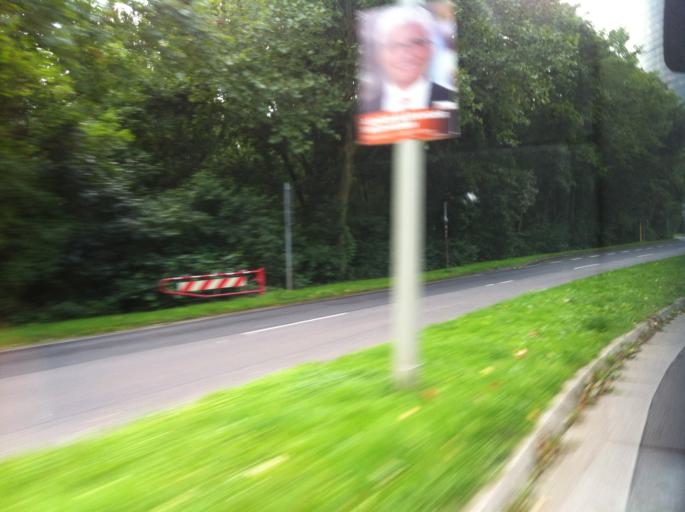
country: DE
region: North Rhine-Westphalia
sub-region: Regierungsbezirk Koln
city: Bonn
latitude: 50.7135
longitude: 7.1339
